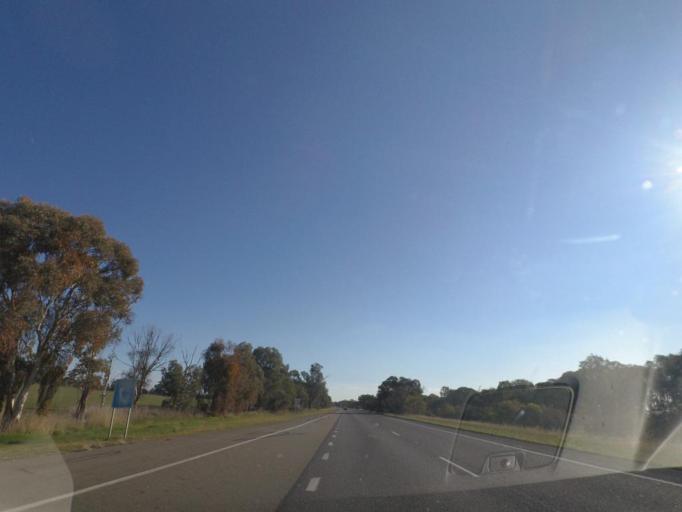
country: AU
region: Victoria
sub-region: Benalla
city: Benalla
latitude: -36.5010
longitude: 146.0990
